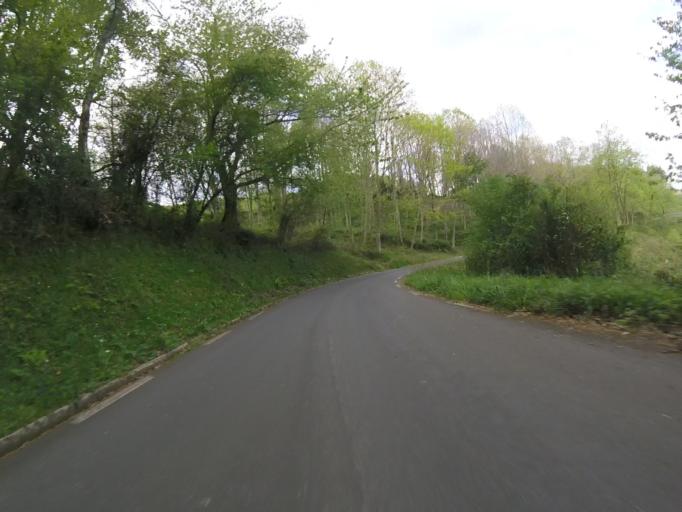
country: ES
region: Basque Country
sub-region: Provincia de Guipuzcoa
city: Zarautz
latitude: 43.2669
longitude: -2.1665
